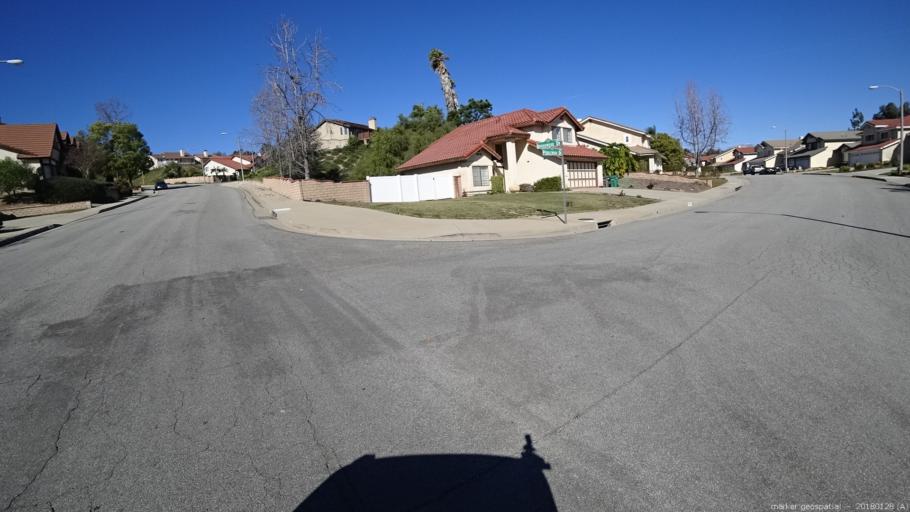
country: US
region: California
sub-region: San Bernardino County
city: Chino Hills
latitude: 33.9992
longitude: -117.7915
